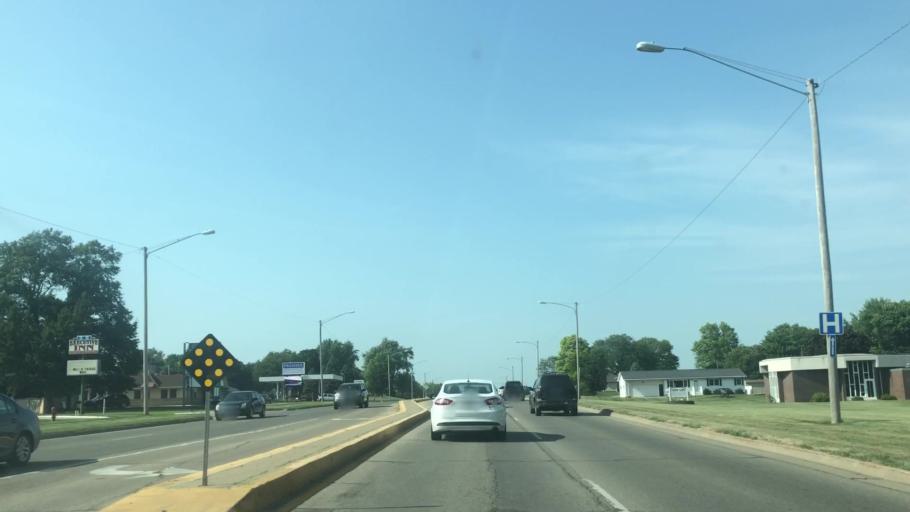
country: US
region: Iowa
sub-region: Marshall County
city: Marshalltown
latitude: 42.0221
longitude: -92.9124
